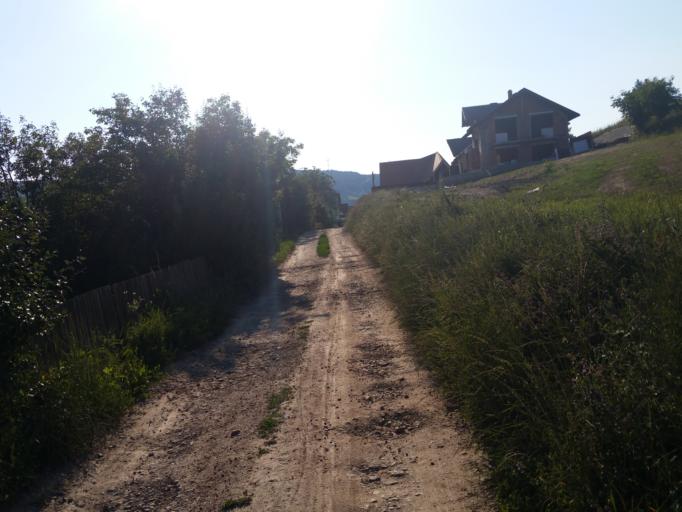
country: RO
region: Cluj
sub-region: Comuna Baciu
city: Baciu
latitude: 46.7871
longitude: 23.5342
